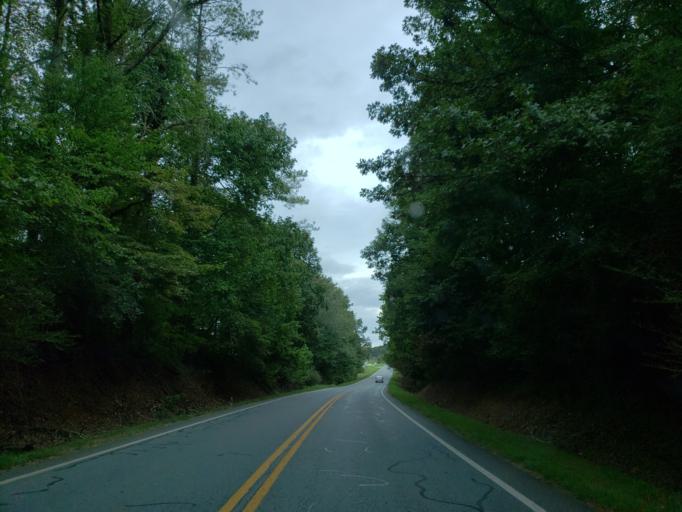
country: US
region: Georgia
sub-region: Gilmer County
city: Ellijay
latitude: 34.6383
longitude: -84.5274
